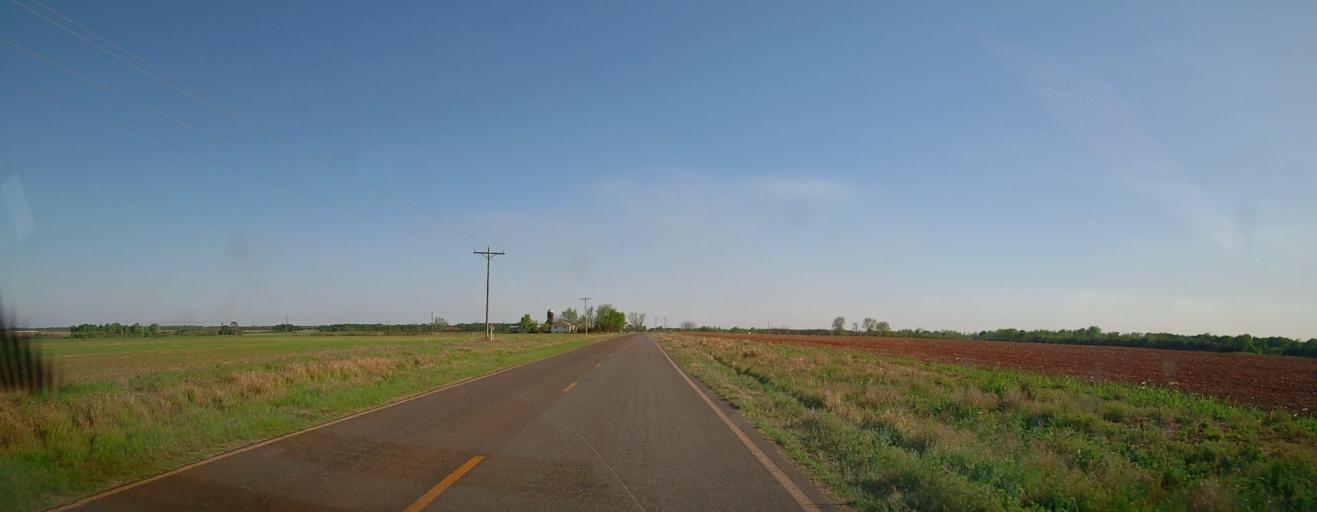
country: US
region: Georgia
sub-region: Macon County
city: Montezuma
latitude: 32.3448
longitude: -83.9438
